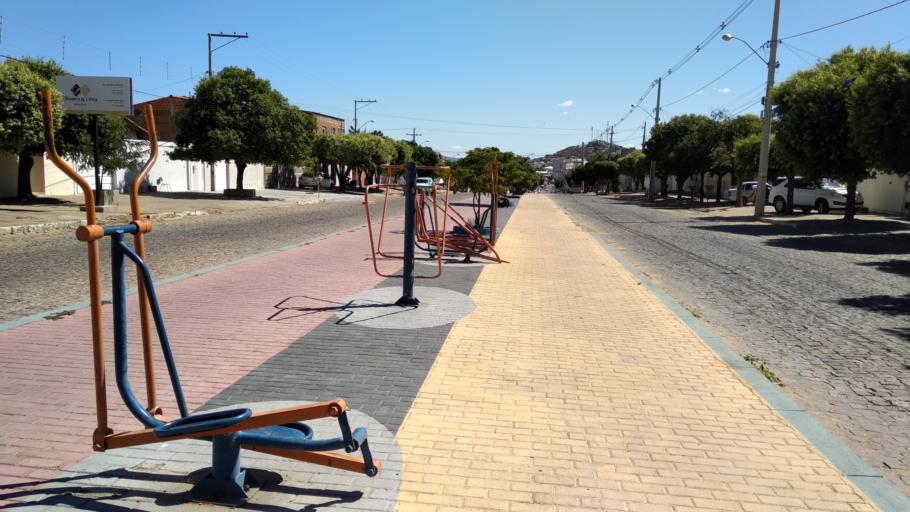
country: BR
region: Bahia
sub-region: Guanambi
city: Guanambi
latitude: -14.2368
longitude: -42.7767
